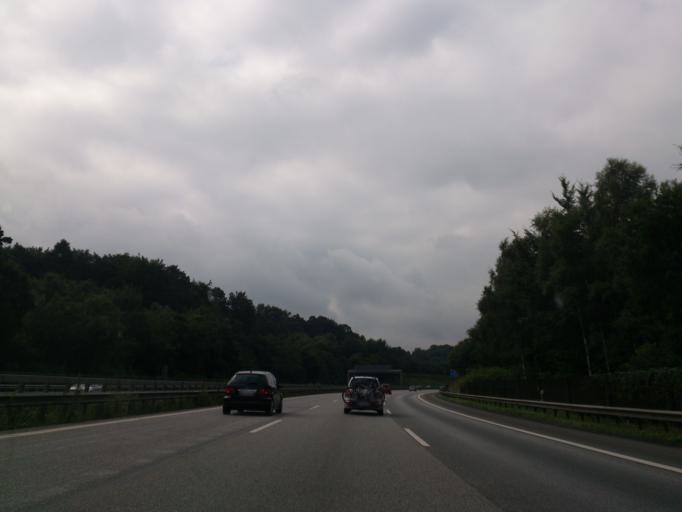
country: DE
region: Hamburg
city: Harburg
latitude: 53.4601
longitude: 9.9284
